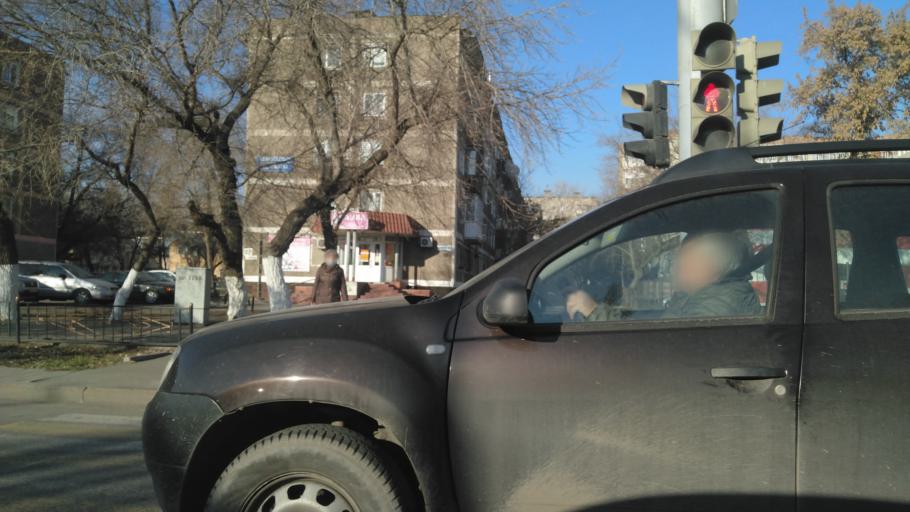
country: KZ
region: Pavlodar
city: Pavlodar
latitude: 52.2905
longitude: 76.9432
